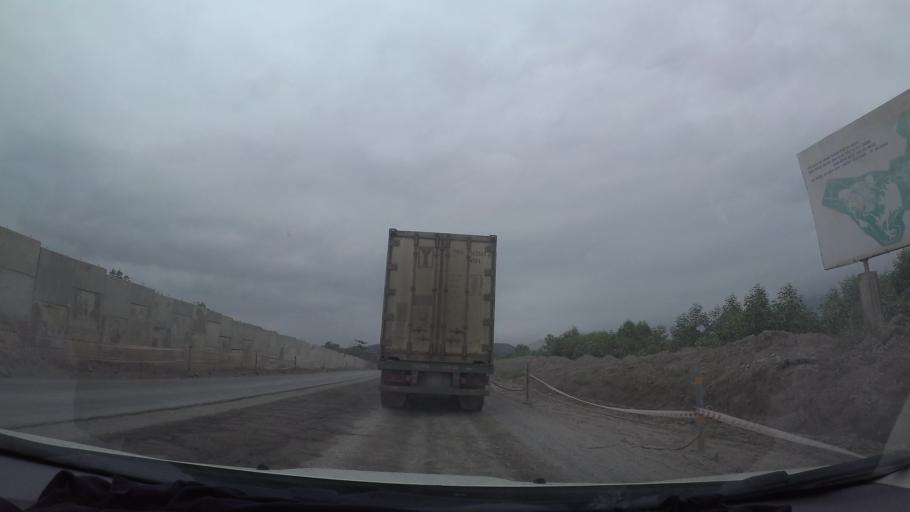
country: VN
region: Da Nang
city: Lien Chieu
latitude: 16.0920
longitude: 108.0864
